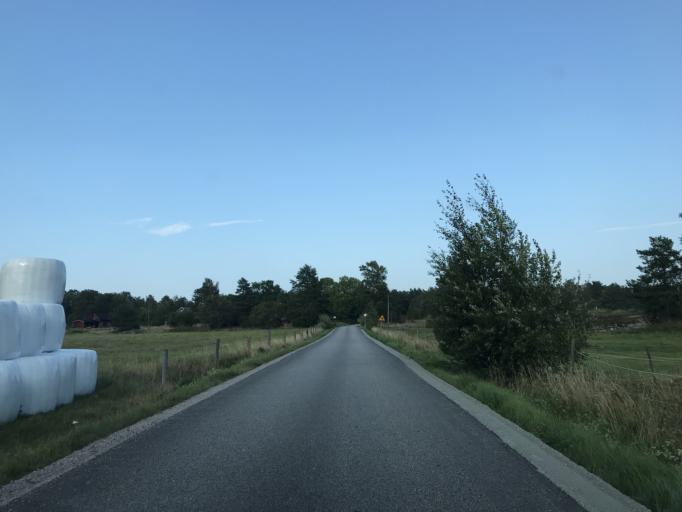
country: SE
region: Stockholm
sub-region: Norrtalje Kommun
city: Bjorko
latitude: 59.8555
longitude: 19.0197
